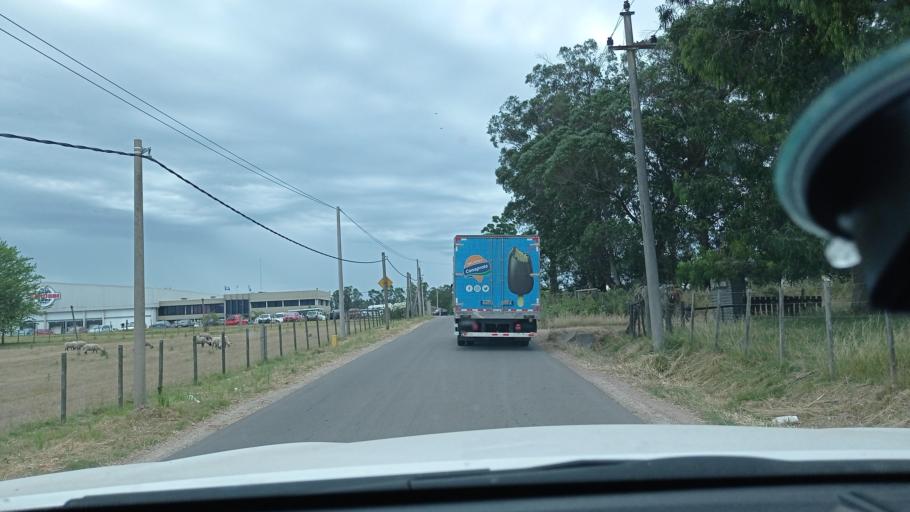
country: UY
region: Canelones
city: La Paz
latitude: -34.8045
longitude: -56.1871
